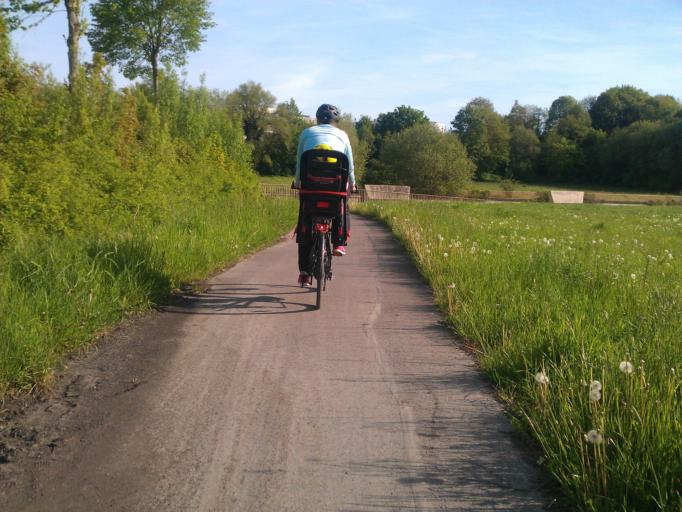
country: DE
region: North Rhine-Westphalia
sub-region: Regierungsbezirk Koln
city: Aachen
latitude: 50.7923
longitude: 6.0570
